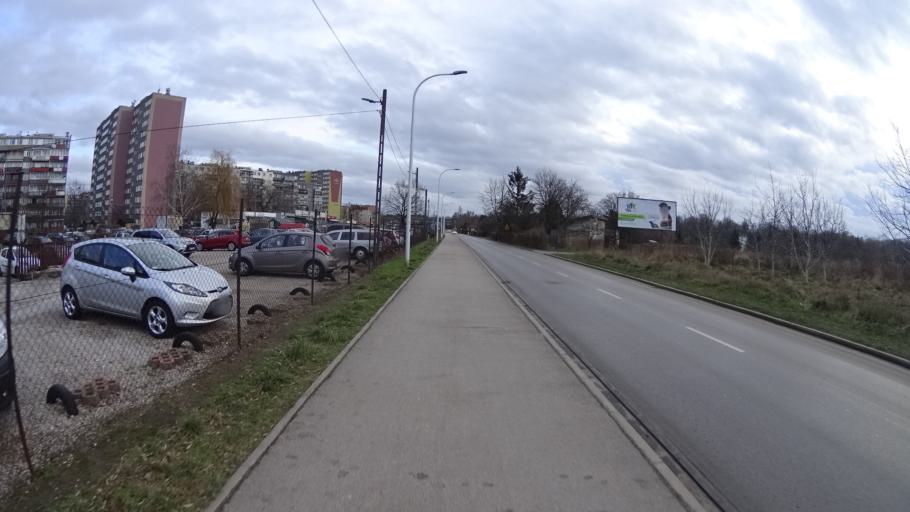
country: PL
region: Masovian Voivodeship
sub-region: Powiat pruszkowski
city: Granica
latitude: 52.1559
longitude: 20.7862
